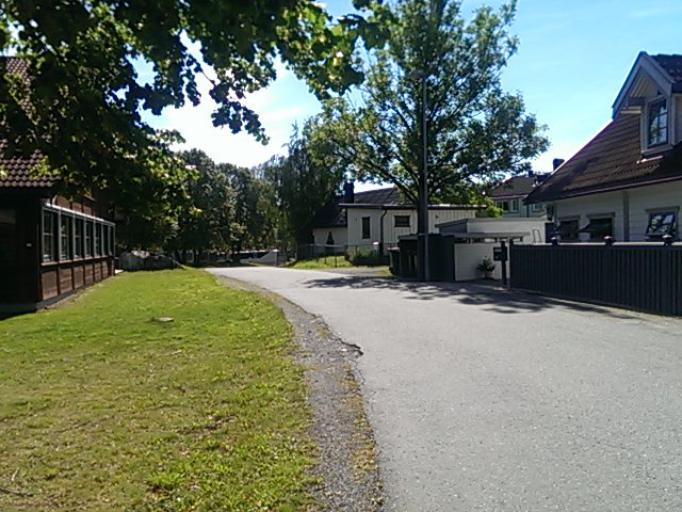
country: NO
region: Buskerud
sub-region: Kongsberg
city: Kongsberg
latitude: 59.6595
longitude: 9.6561
